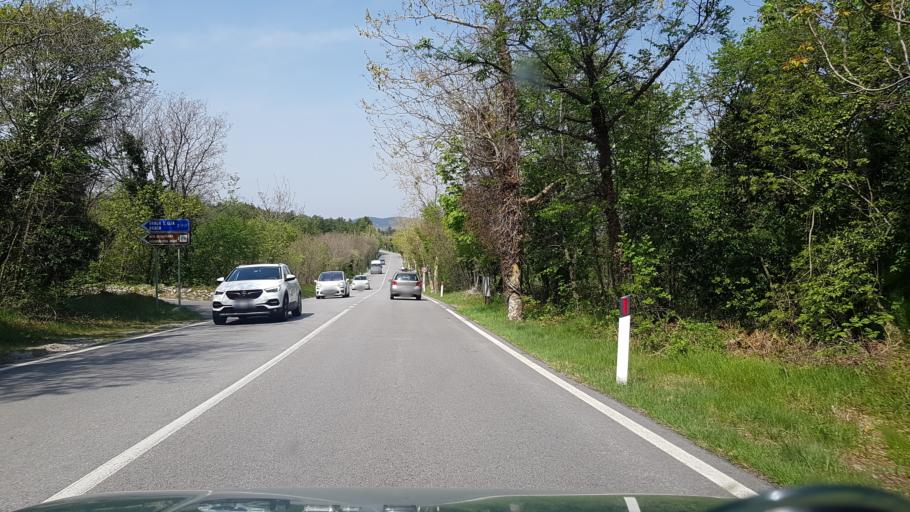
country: IT
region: Friuli Venezia Giulia
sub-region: Provincia di Trieste
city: Dolina
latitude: 45.6369
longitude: 13.8726
